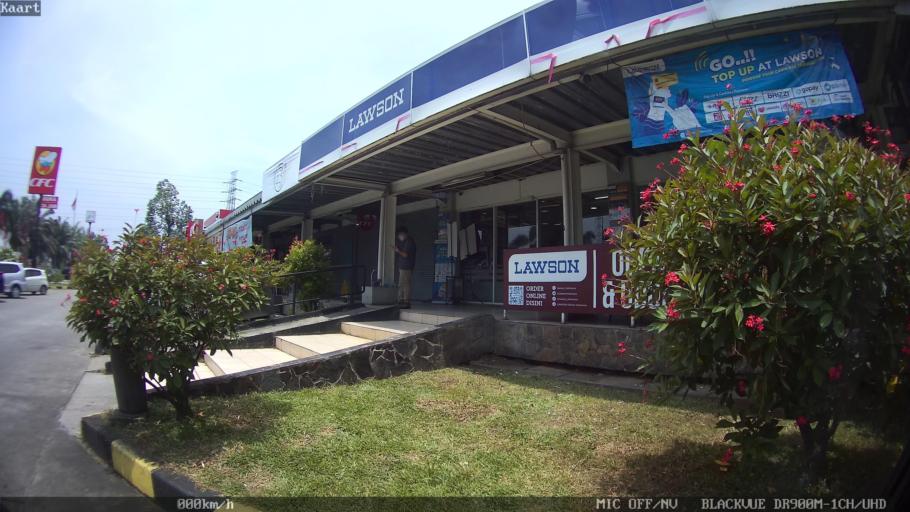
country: ID
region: West Java
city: Kresek
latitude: -6.1937
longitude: 106.4249
